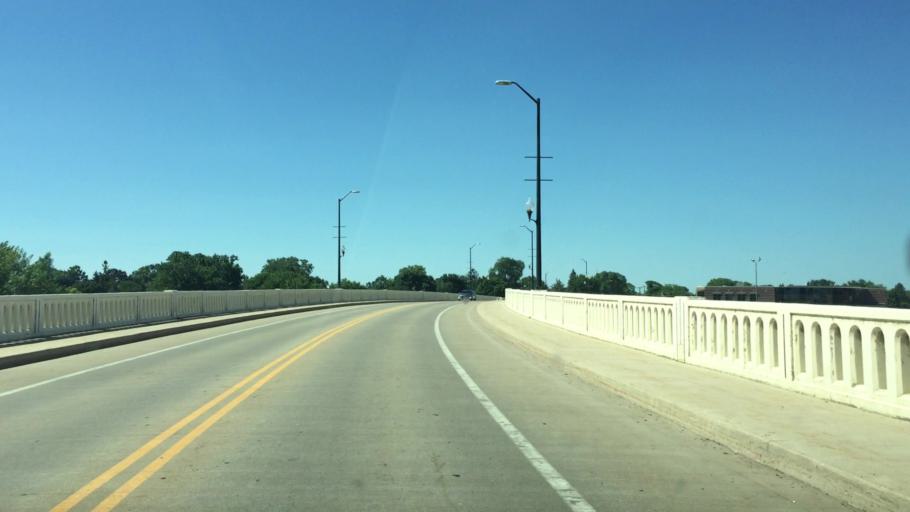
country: US
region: Wisconsin
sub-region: Winnebago County
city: Neenah
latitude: 44.1874
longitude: -88.4550
